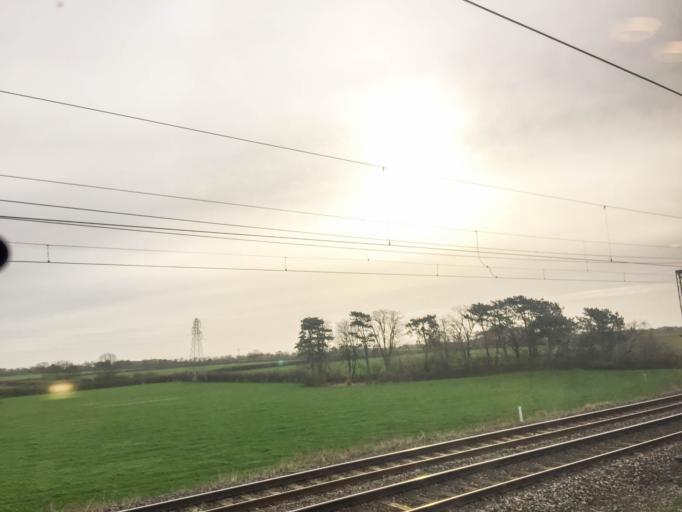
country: GB
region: England
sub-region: Cheshire West and Chester
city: Winsford
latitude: 53.1764
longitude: -2.4828
